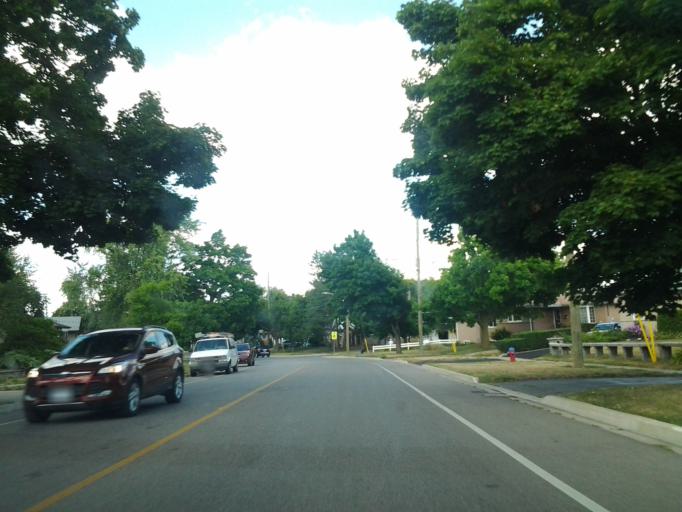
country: CA
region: Ontario
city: Brampton
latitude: 43.6443
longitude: -79.8824
